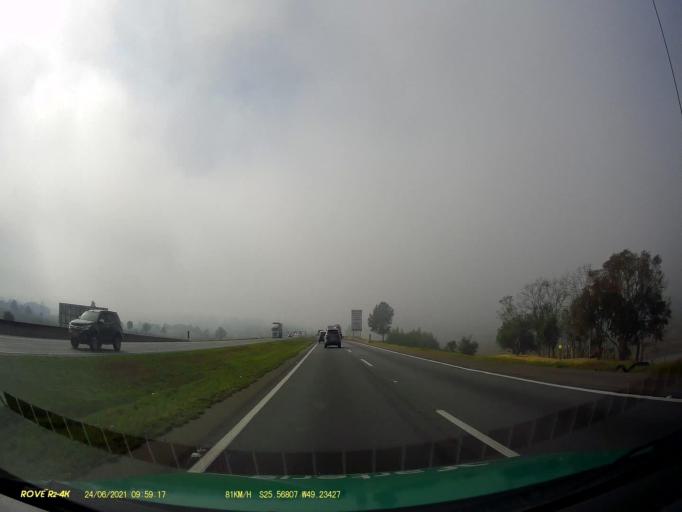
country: BR
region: Parana
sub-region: Sao Jose Dos Pinhais
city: Sao Jose dos Pinhais
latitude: -25.5681
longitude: -49.2343
